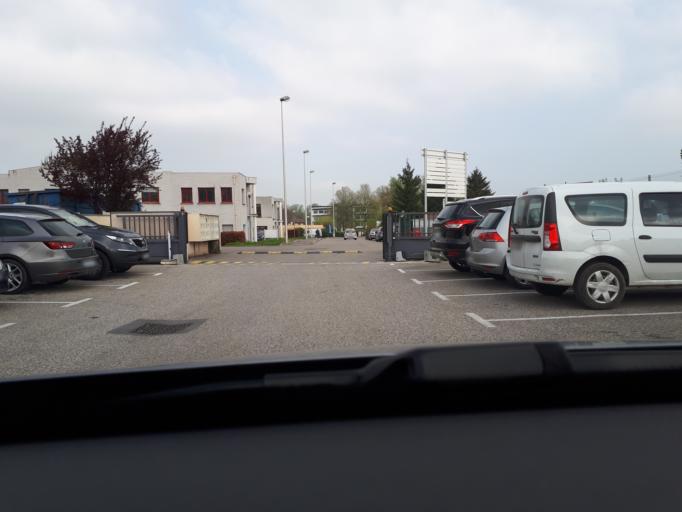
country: FR
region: Rhone-Alpes
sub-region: Departement de l'Isere
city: Bourgoin-Jallieu
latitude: 45.5871
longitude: 5.2608
